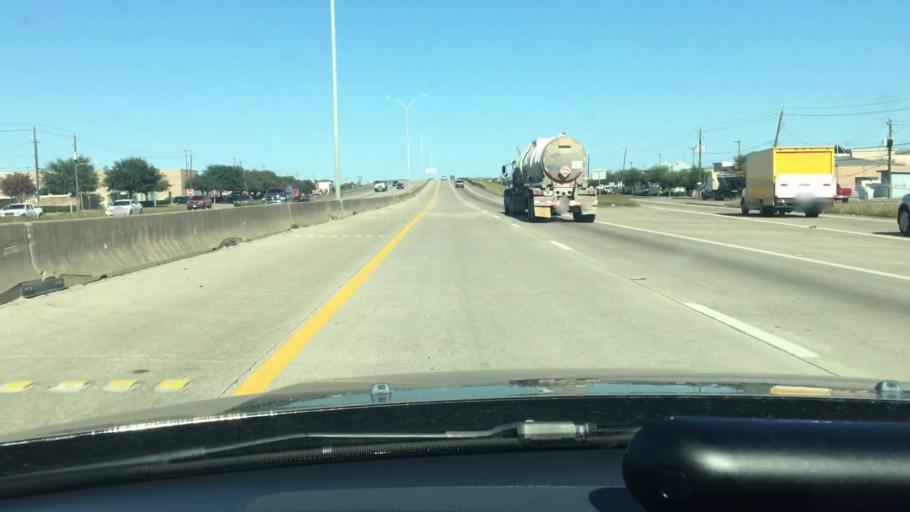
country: US
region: Texas
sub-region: Harris County
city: Cloverleaf
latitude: 29.8041
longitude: -95.1633
